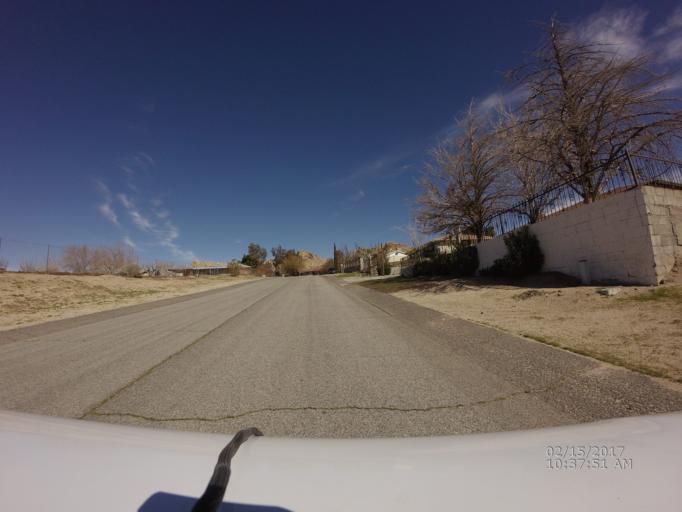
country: US
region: California
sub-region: Los Angeles County
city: Lake Los Angeles
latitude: 34.5850
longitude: -117.8549
